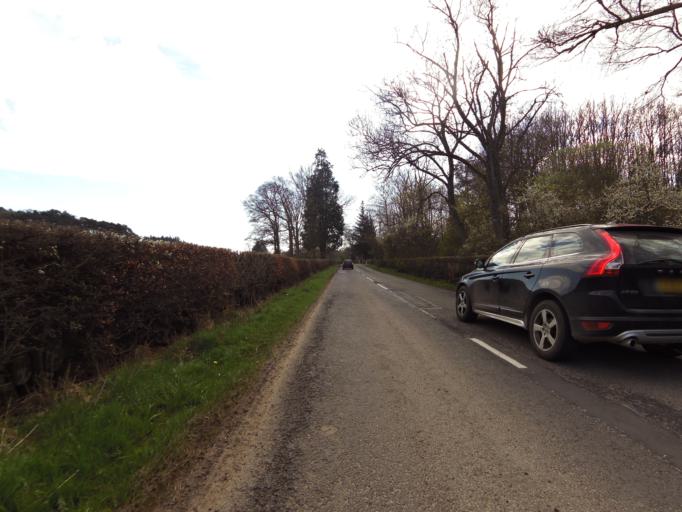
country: GB
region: Scotland
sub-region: Fife
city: Newburgh
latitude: 56.3256
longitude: -3.2294
